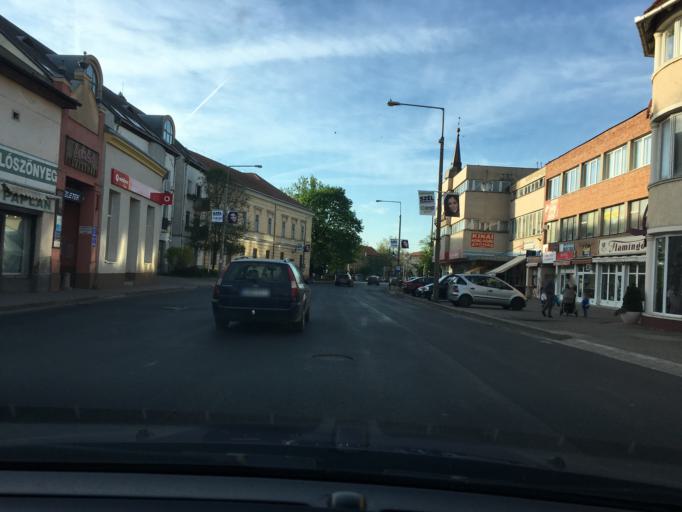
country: HU
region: Hajdu-Bihar
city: Berettyoujfalu
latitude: 47.2214
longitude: 21.5363
